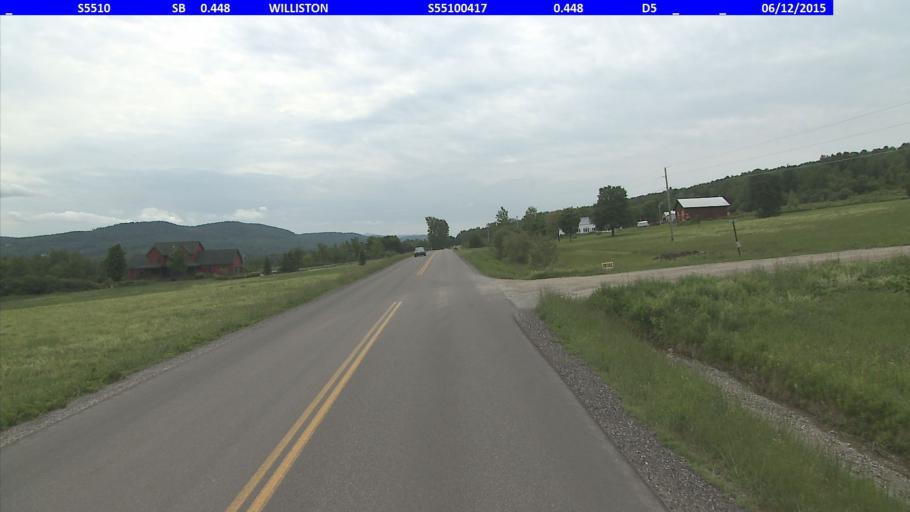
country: US
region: Vermont
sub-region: Chittenden County
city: Hinesburg
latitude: 44.3791
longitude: -73.0960
